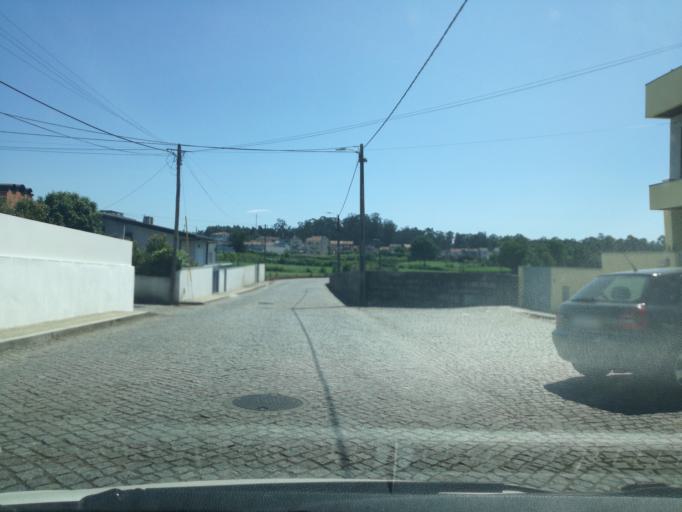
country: PT
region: Porto
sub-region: Maia
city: Anta
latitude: 41.2688
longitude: -8.6326
